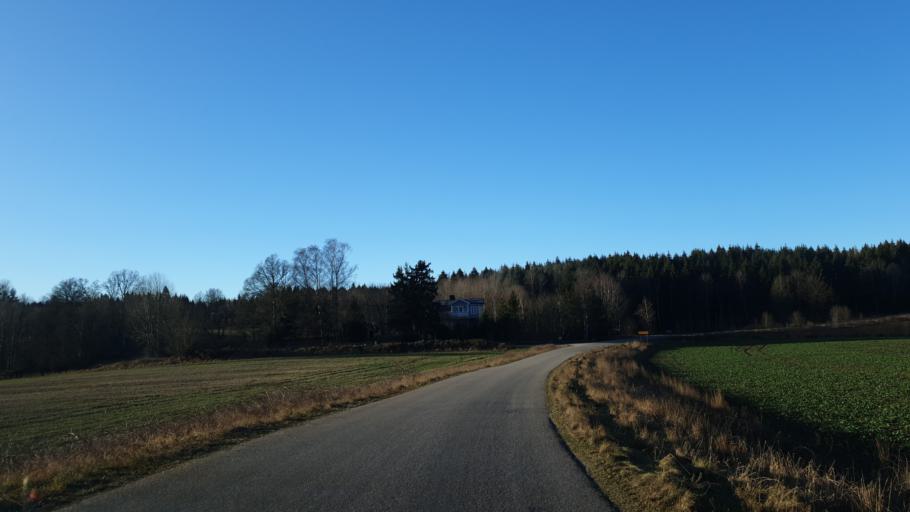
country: SE
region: Blekinge
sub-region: Karlskrona Kommun
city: Nattraby
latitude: 56.2613
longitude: 15.4907
